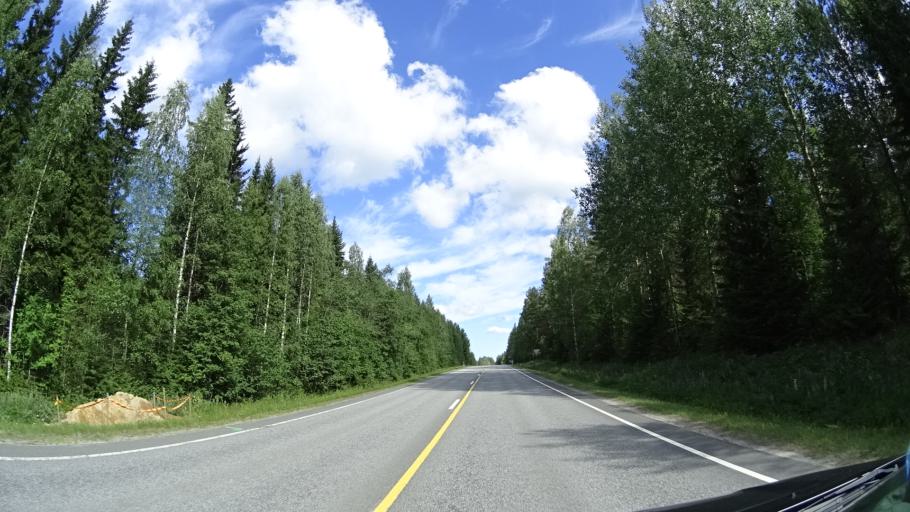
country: FI
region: Pirkanmaa
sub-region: Luoteis-Pirkanmaa
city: Kihnioe
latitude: 62.1860
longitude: 23.1725
